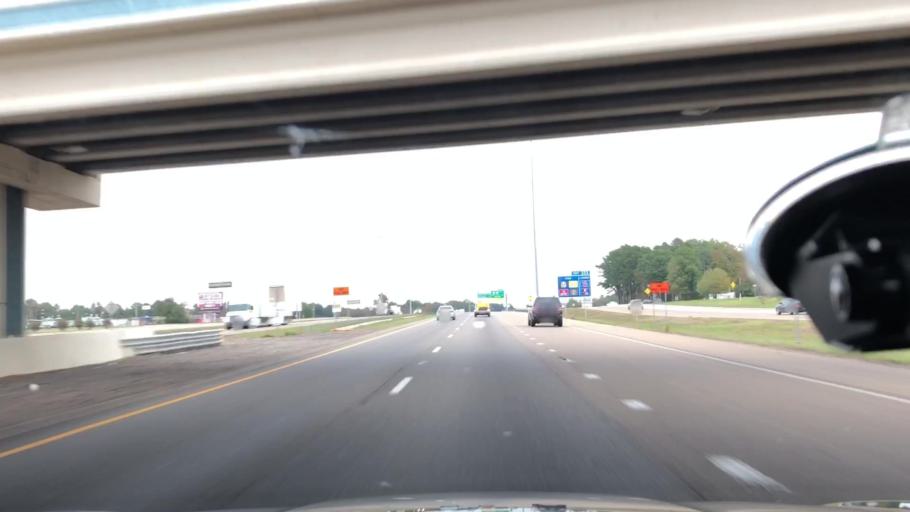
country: US
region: Arkansas
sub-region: Miller County
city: Texarkana
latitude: 33.4654
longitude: -94.0664
